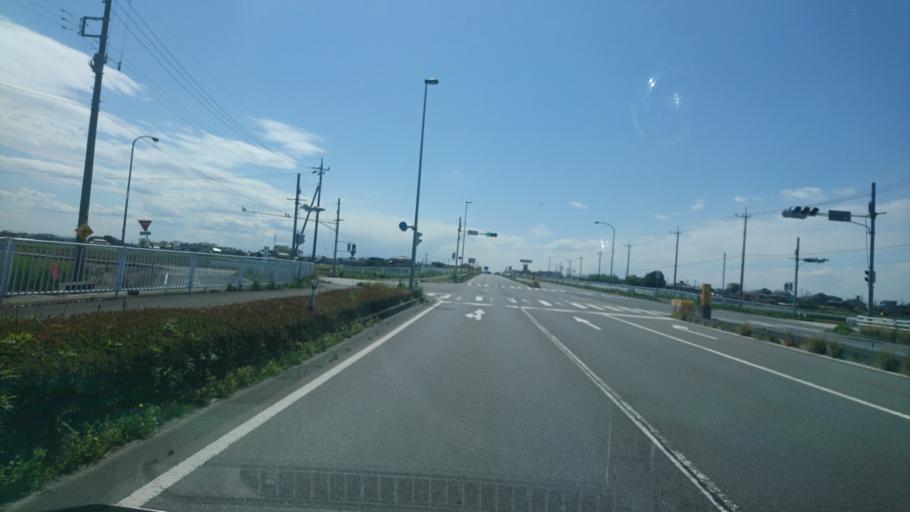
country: JP
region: Ibaraki
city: Yuki
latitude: 36.2897
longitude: 139.8890
